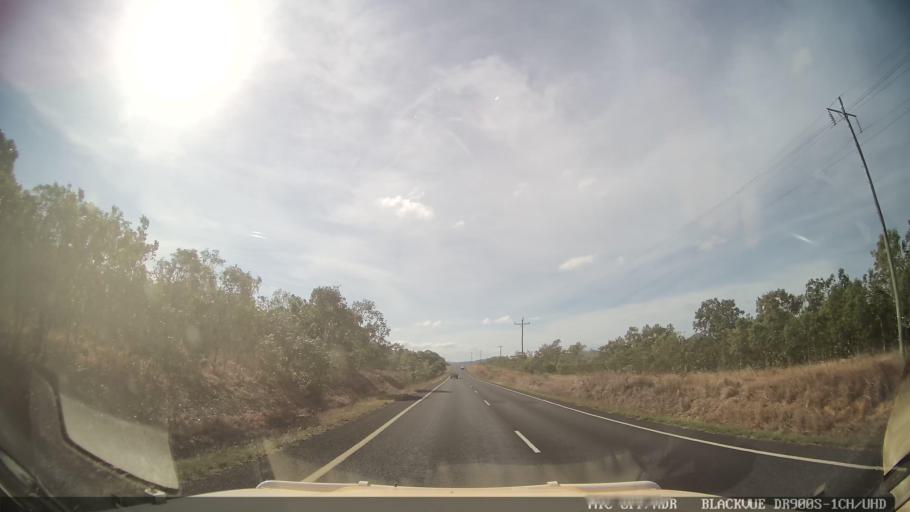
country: AU
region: Queensland
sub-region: Cook
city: Cooktown
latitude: -15.5483
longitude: 145.2417
